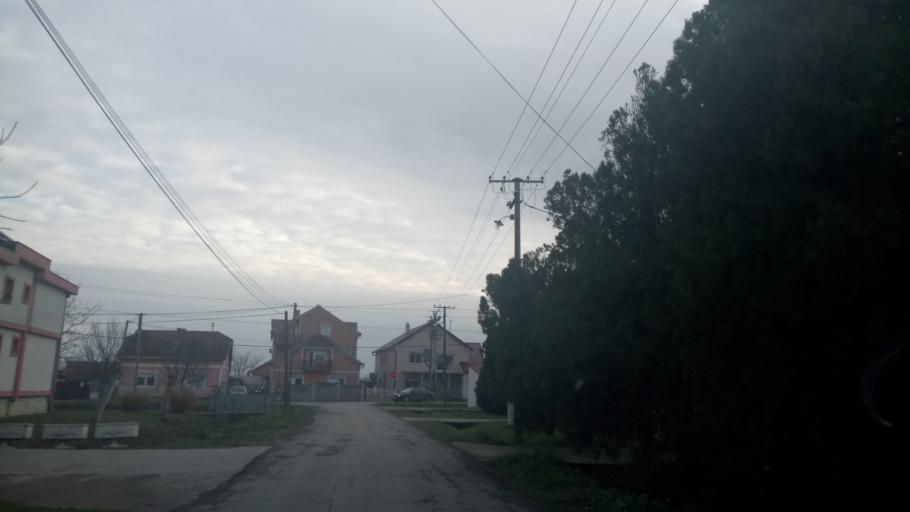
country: RS
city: Vojka
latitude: 44.9309
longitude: 20.1539
